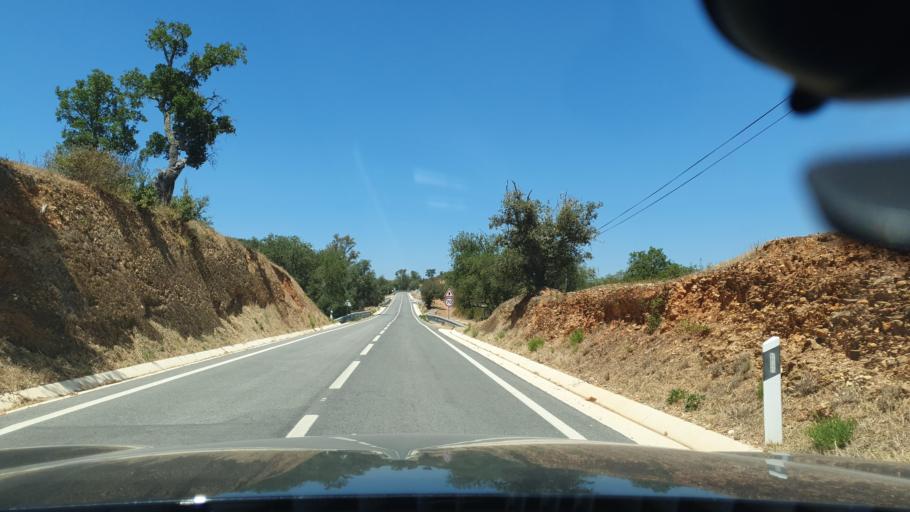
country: PT
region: Beja
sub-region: Odemira
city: Odemira
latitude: 37.5167
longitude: -8.4754
